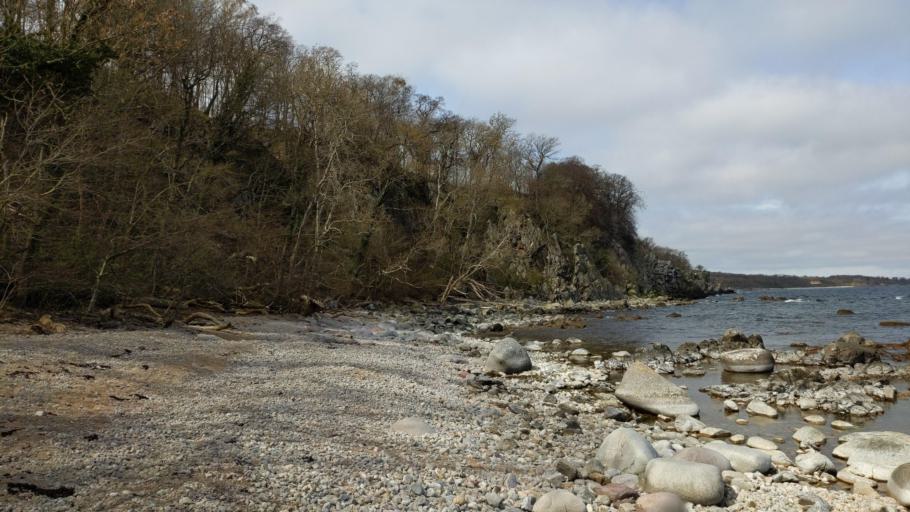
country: DK
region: Capital Region
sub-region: Bornholm Kommune
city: Akirkeby
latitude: 55.2226
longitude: 14.9058
